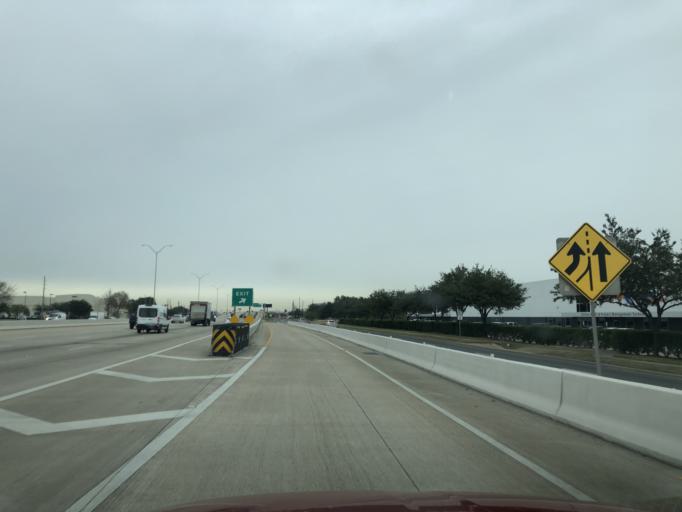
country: US
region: Texas
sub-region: Fort Bend County
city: Missouri City
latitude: 29.6394
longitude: -95.5331
